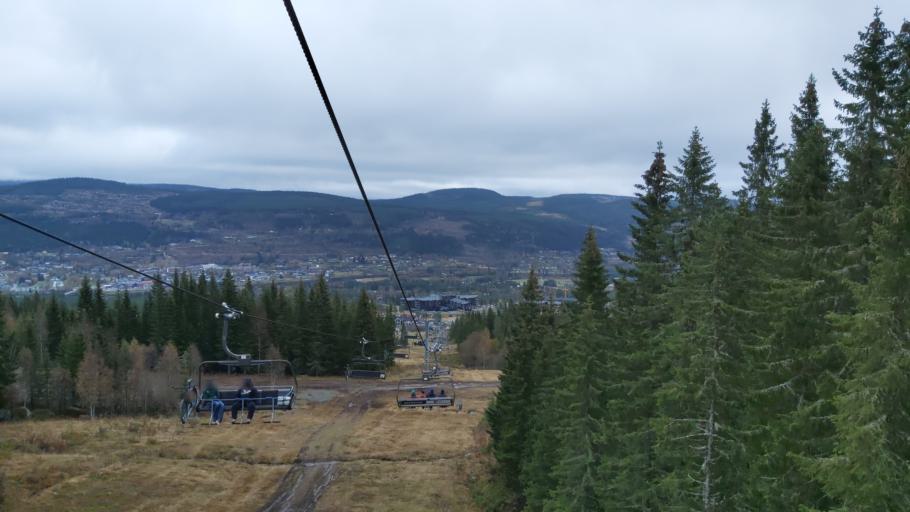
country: NO
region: Hedmark
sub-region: Trysil
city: Innbygda
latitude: 61.3082
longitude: 12.2248
